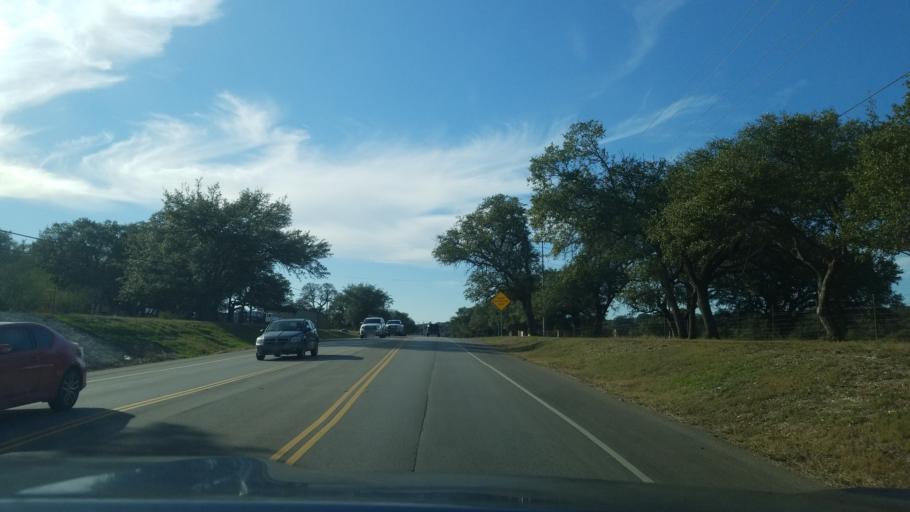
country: US
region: Texas
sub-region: Comal County
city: Canyon Lake
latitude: 29.7736
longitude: -98.2909
